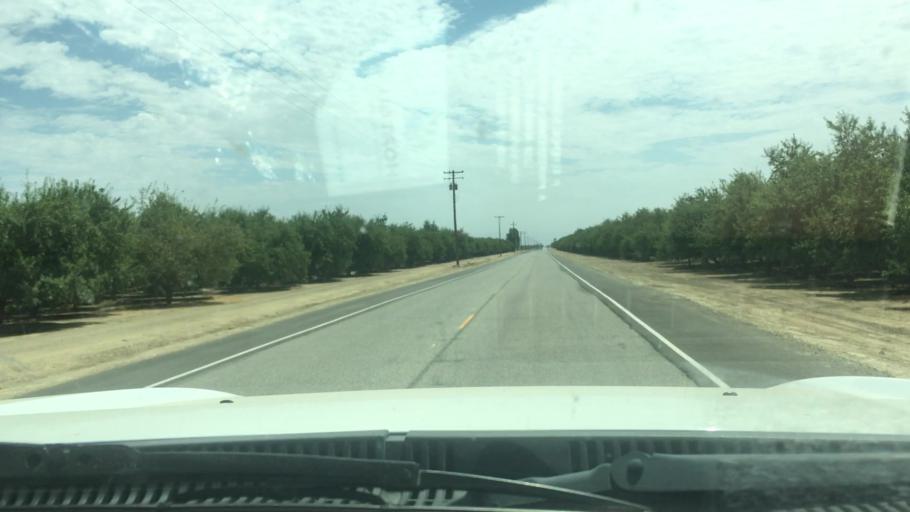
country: US
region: California
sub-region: Kern County
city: Wasco
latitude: 35.5578
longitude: -119.4272
